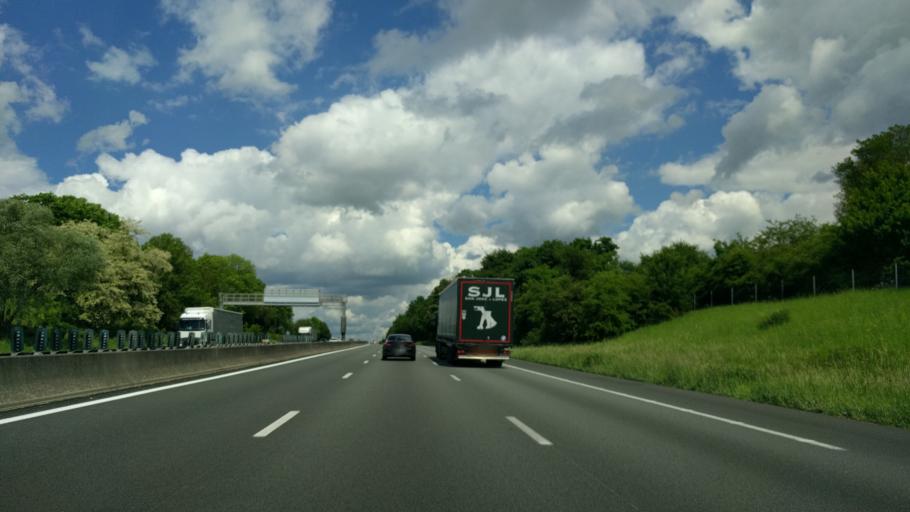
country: FR
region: Picardie
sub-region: Departement de l'Oise
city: Longueil-Sainte-Marie
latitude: 49.3516
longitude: 2.7013
